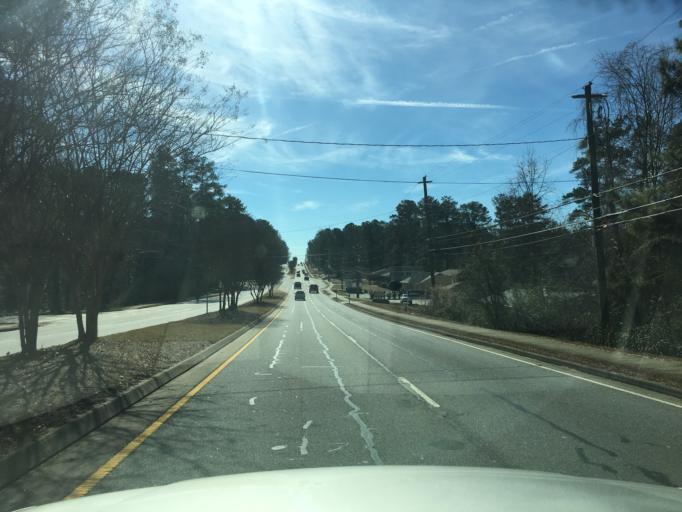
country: US
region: Georgia
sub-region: Gwinnett County
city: Lawrenceville
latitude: 33.9375
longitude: -83.9937
